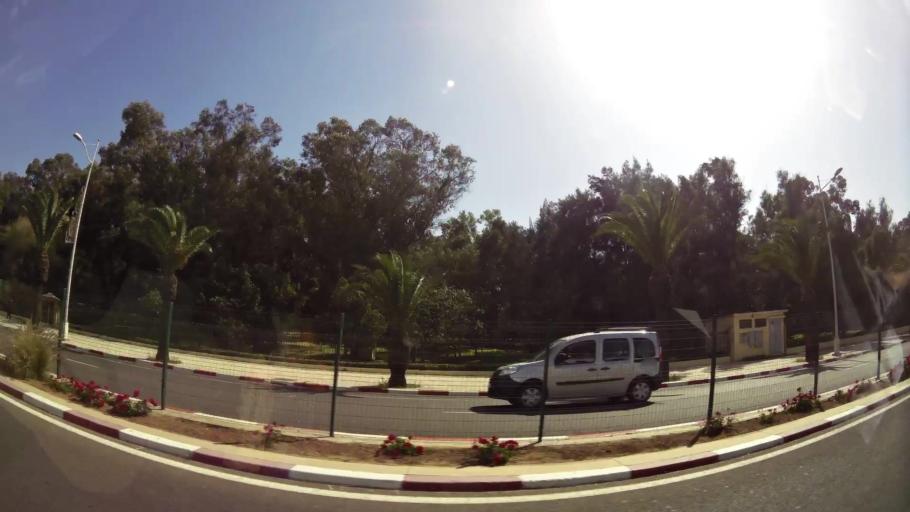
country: MA
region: Souss-Massa-Draa
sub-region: Agadir-Ida-ou-Tnan
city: Agadir
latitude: 30.4101
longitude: -9.5916
